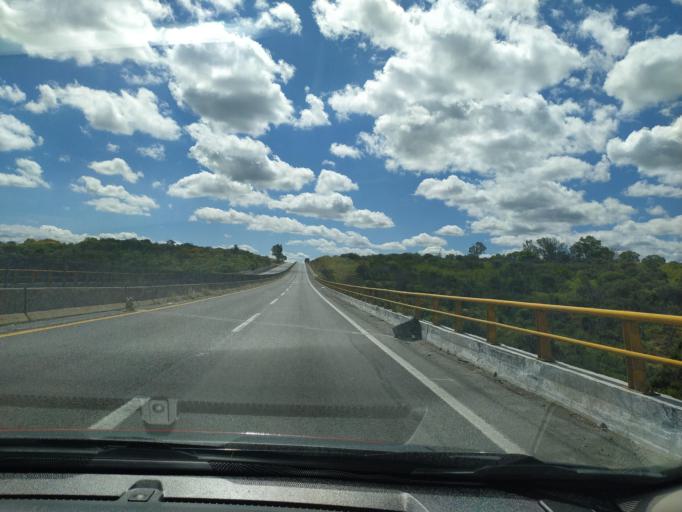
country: MX
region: Jalisco
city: Valle de Guadalupe
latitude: 20.9274
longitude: -102.6655
